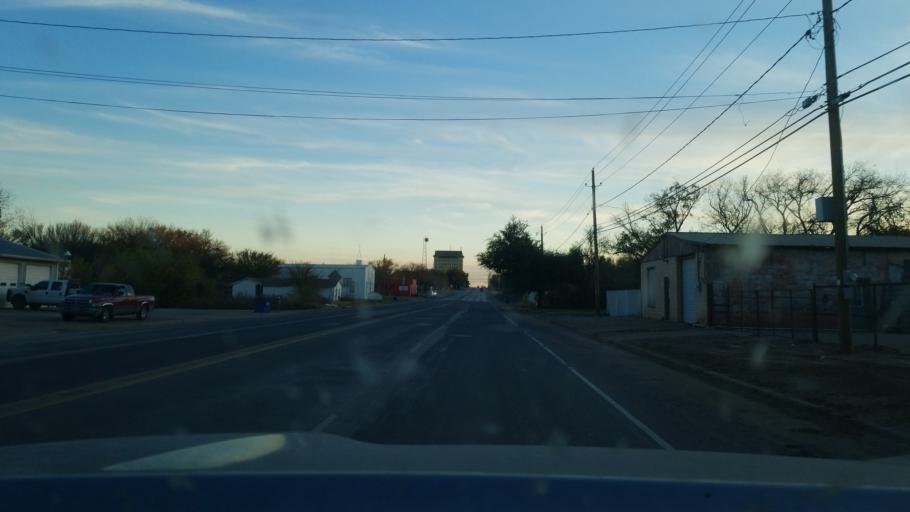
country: US
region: Texas
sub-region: Stephens County
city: Breckenridge
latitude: 32.7621
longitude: -98.9027
